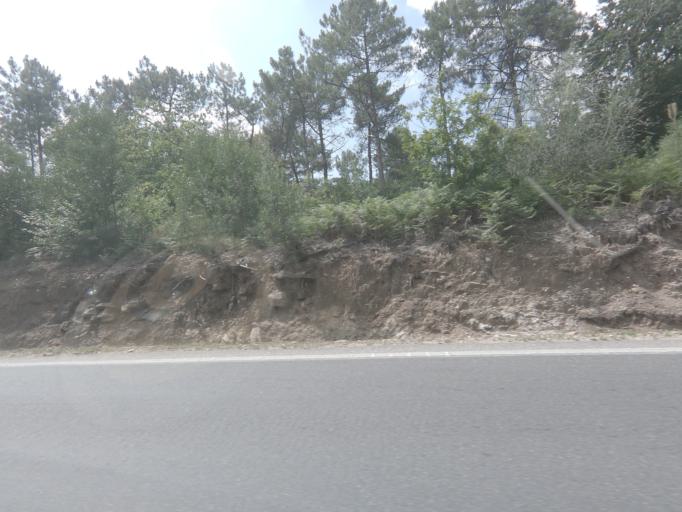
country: PT
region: Viana do Castelo
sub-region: Valenca
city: Valenca
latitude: 42.0325
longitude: -8.6704
